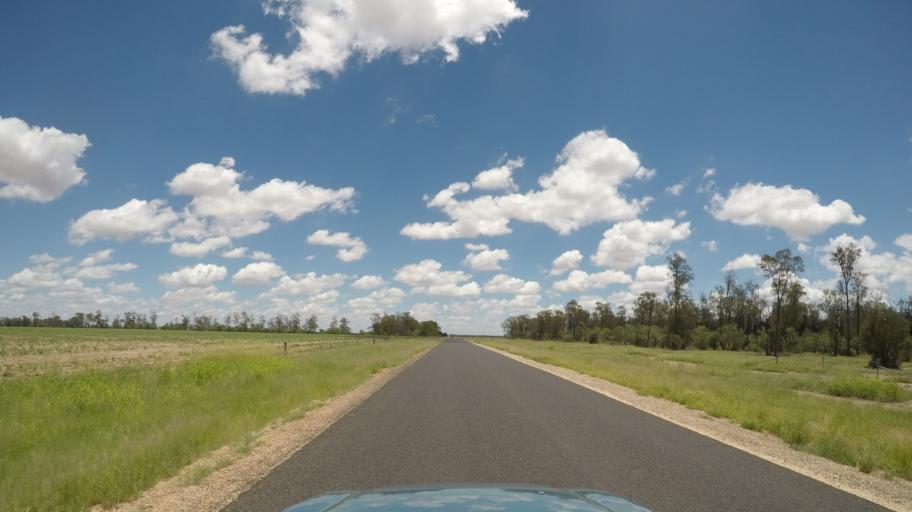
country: AU
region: Queensland
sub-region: Goondiwindi
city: Goondiwindi
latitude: -28.1727
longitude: 150.2325
